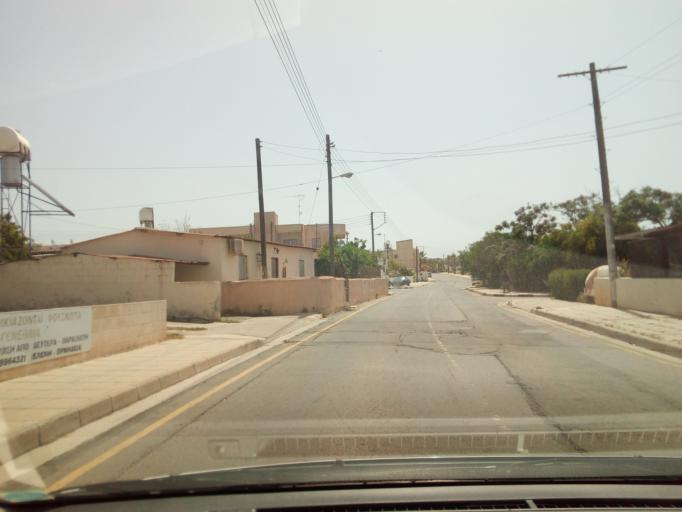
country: CY
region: Larnaka
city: Xylotymbou
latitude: 34.9919
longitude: 33.7843
